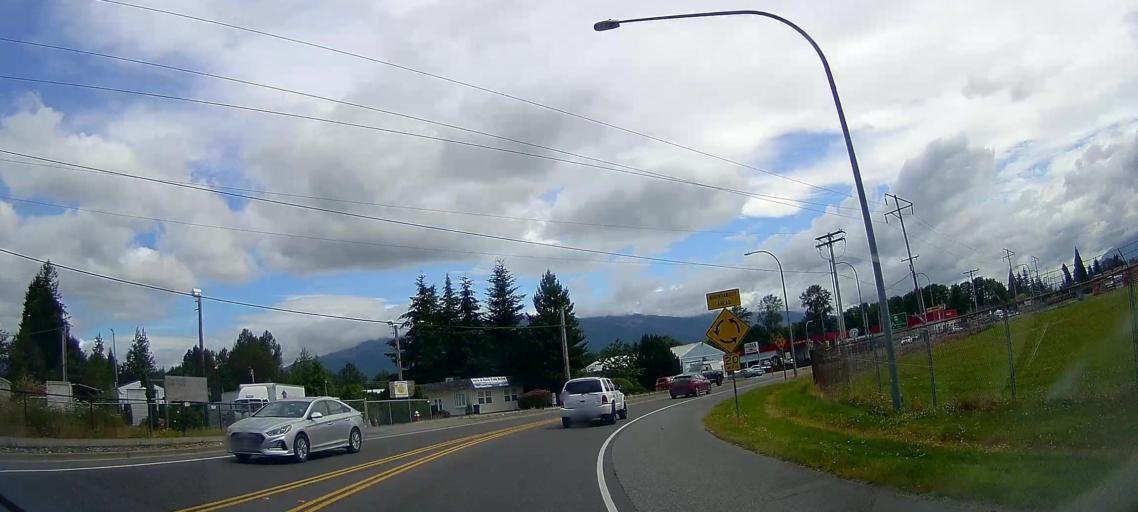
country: US
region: Washington
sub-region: Skagit County
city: Sedro-Woolley
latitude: 48.5105
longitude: -122.2439
